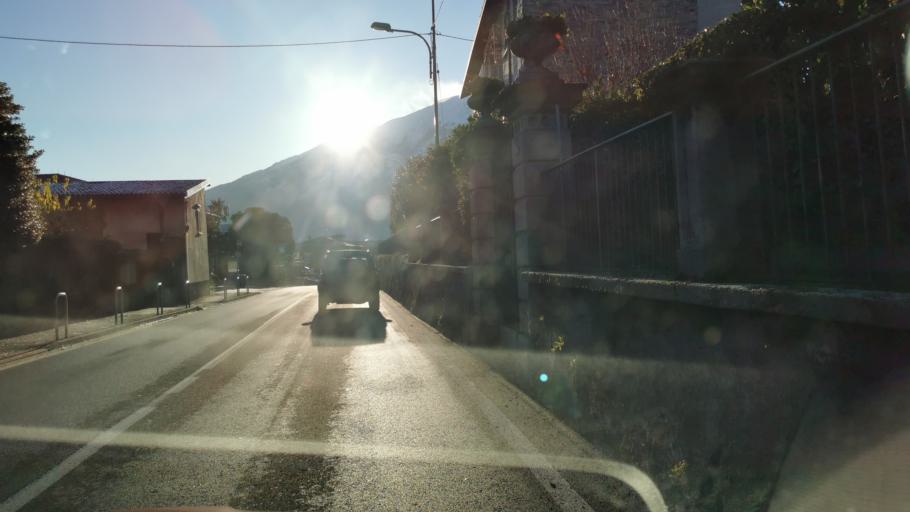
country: IT
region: Lombardy
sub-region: Provincia di Como
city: Gravedona-San Gregorio
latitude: 46.1452
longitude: 9.3010
